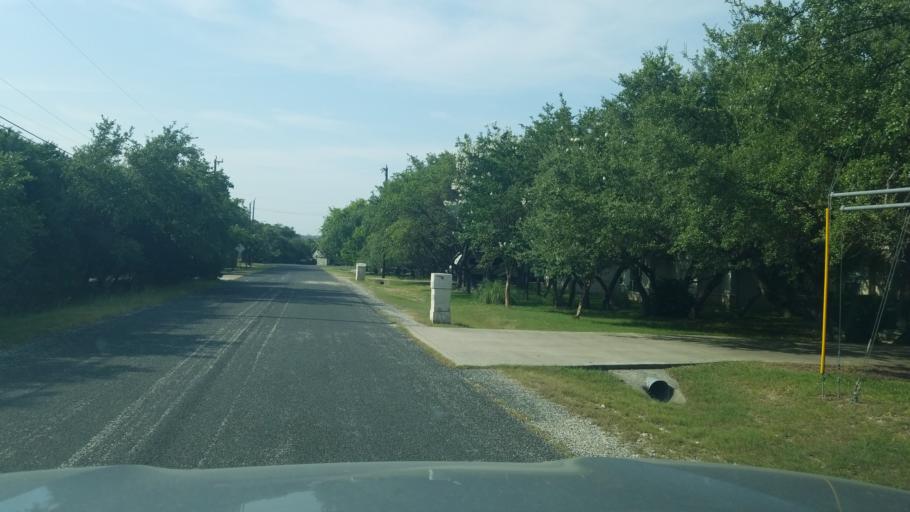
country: US
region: Texas
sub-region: Bexar County
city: Timberwood Park
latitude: 29.6968
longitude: -98.4939
